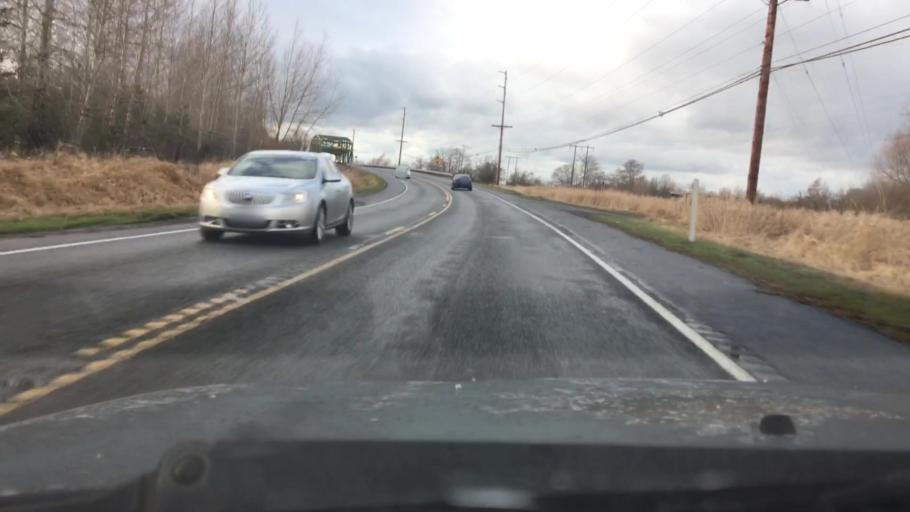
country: US
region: Washington
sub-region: Whatcom County
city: Ferndale
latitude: 48.8187
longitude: -122.5759
